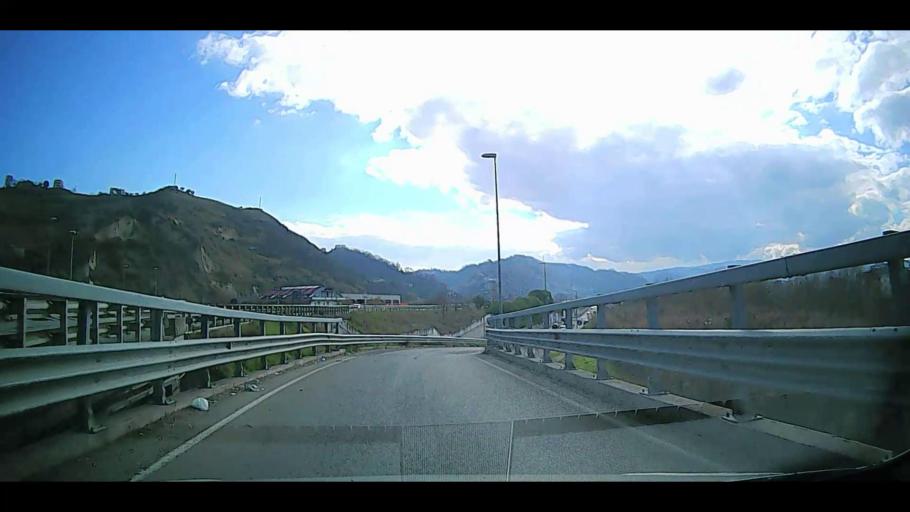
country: IT
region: Calabria
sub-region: Provincia di Cosenza
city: Cosenza
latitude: 39.3111
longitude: 16.2621
